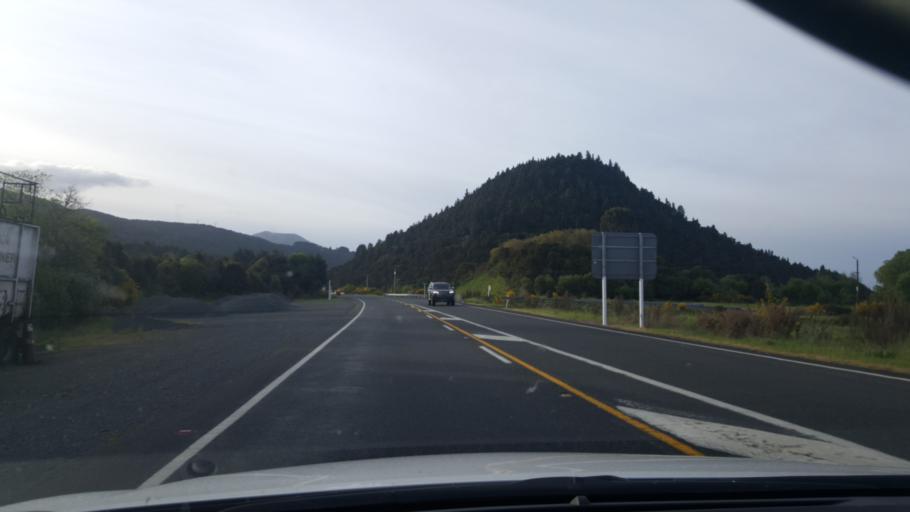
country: NZ
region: Waikato
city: Turangi
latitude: -38.9811
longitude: 175.7787
